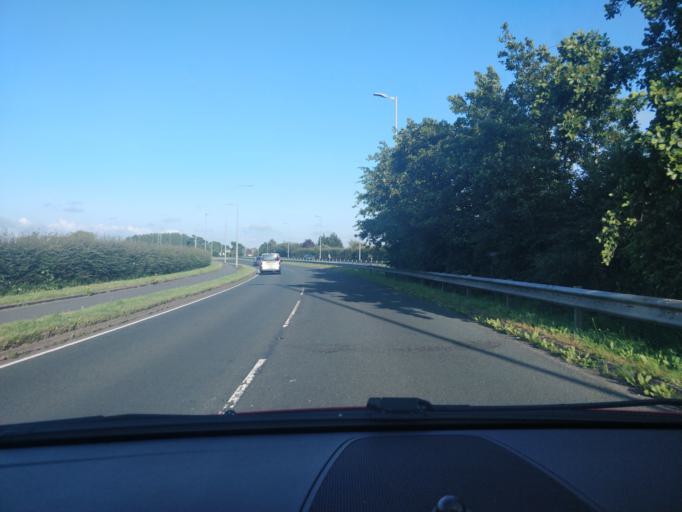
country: GB
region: England
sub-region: Lancashire
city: Banks
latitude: 53.6635
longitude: -2.8915
